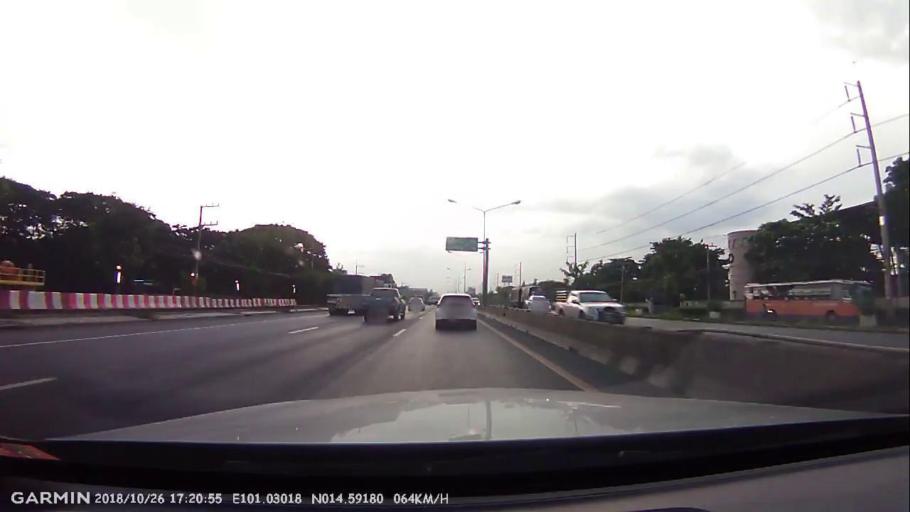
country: TH
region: Sara Buri
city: Kaeng Khoi
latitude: 14.5917
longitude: 101.0300
